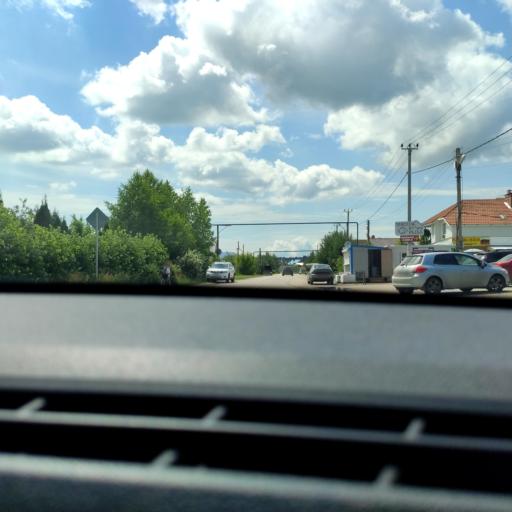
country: RU
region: Samara
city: Podstepki
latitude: 53.5708
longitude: 49.0811
